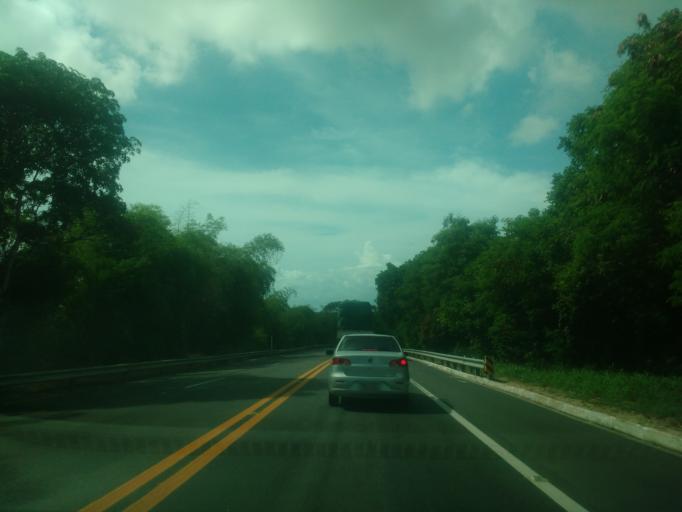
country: BR
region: Alagoas
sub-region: Marechal Deodoro
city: Marechal Deodoro
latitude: -9.6905
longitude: -35.8164
